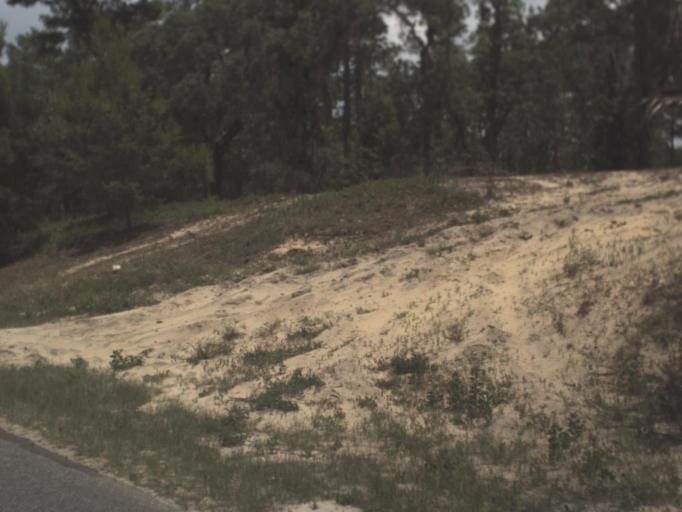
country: US
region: Florida
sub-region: Putnam County
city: Crescent City
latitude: 29.4283
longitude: -81.7374
